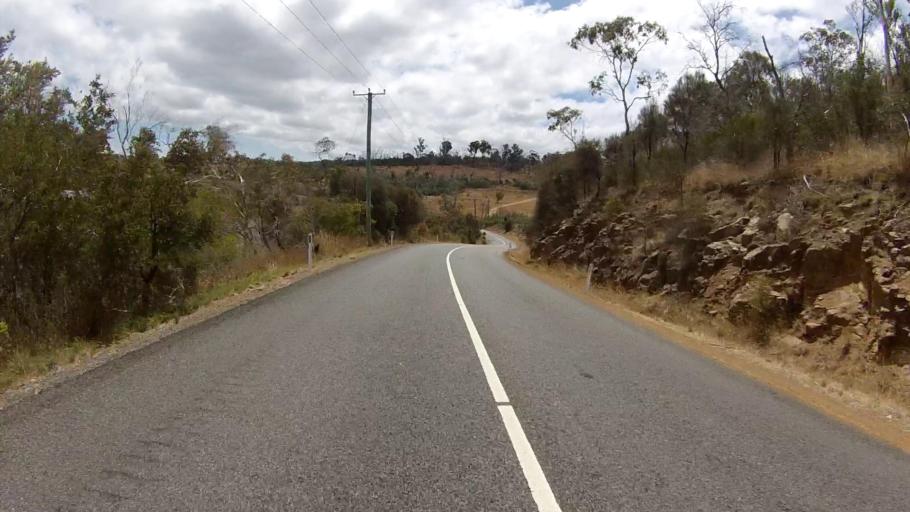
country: AU
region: Tasmania
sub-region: Sorell
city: Sorell
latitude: -42.8651
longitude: 147.6917
